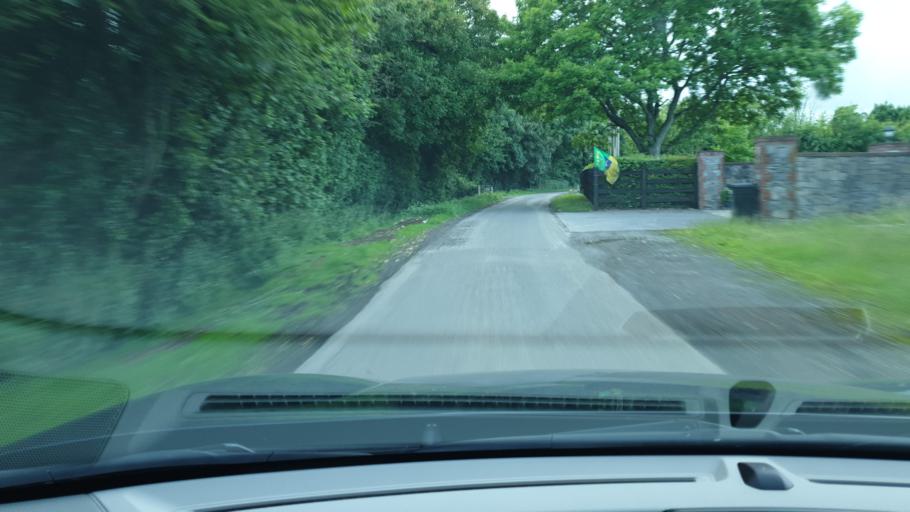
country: IE
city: Kentstown
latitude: 53.5722
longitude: -6.5063
